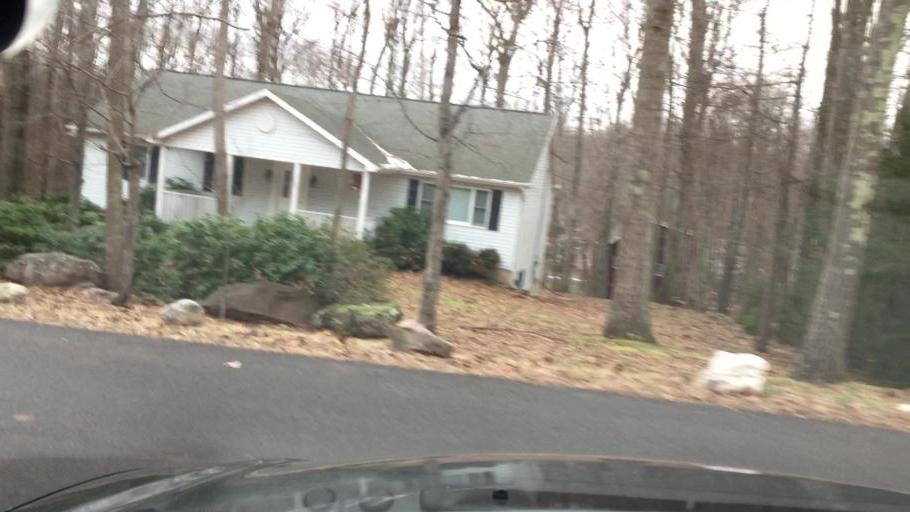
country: US
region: Pennsylvania
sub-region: Luzerne County
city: Freeland
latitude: 41.0364
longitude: -75.9371
